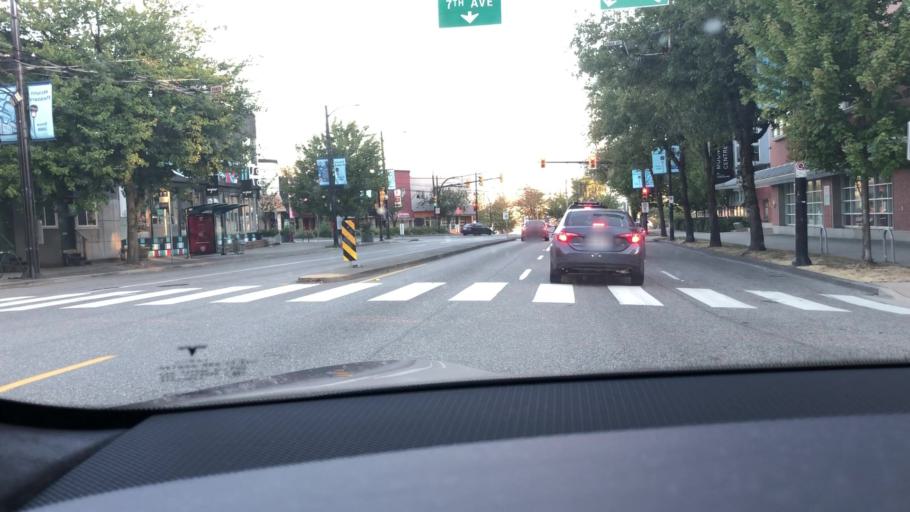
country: CA
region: British Columbia
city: Vancouver
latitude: 49.2636
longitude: -123.1002
